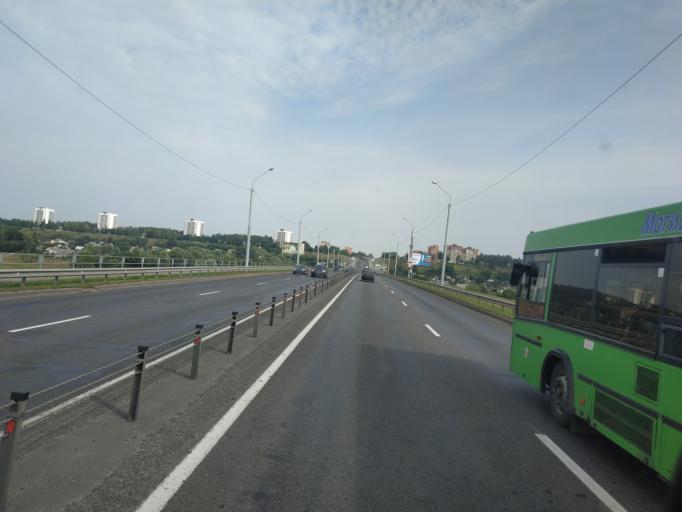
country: BY
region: Mogilev
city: Mahilyow
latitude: 53.8936
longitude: 30.3736
